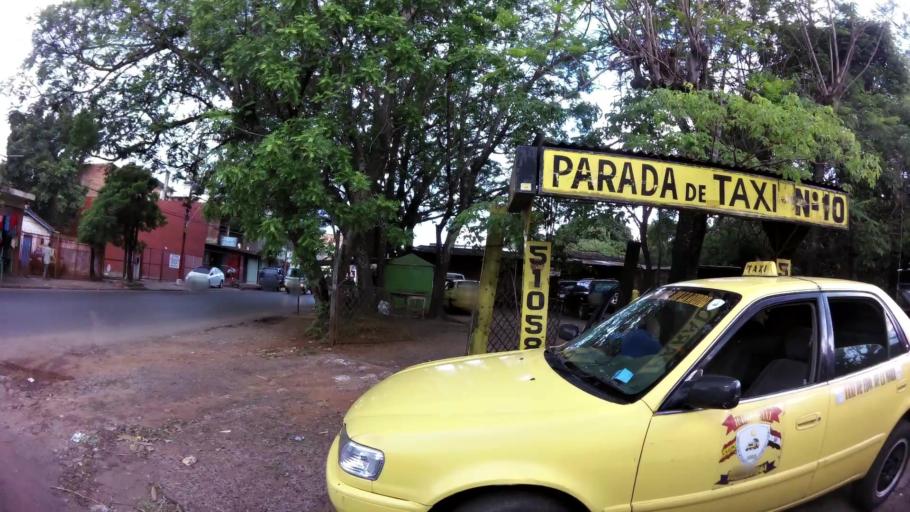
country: PY
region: Central
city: Fernando de la Mora
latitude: -25.3380
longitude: -57.5597
